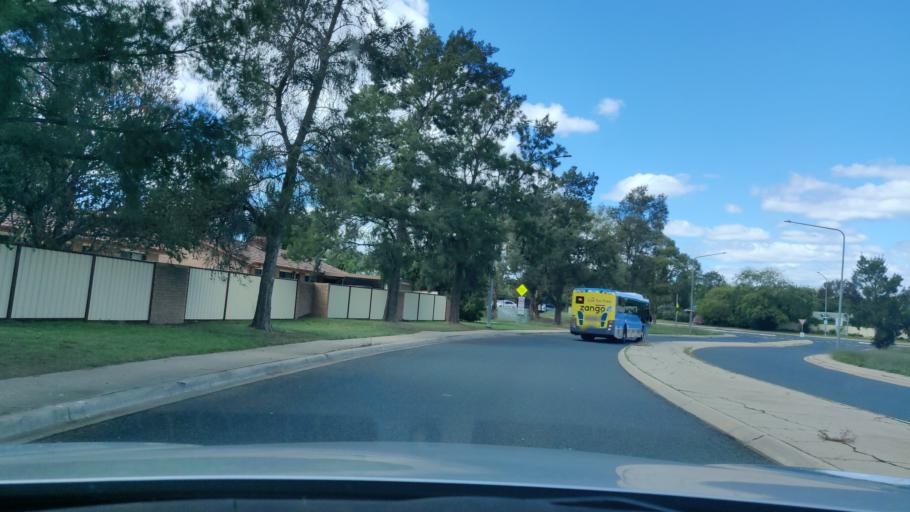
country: AU
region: Australian Capital Territory
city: Macarthur
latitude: -35.4286
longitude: 149.0876
